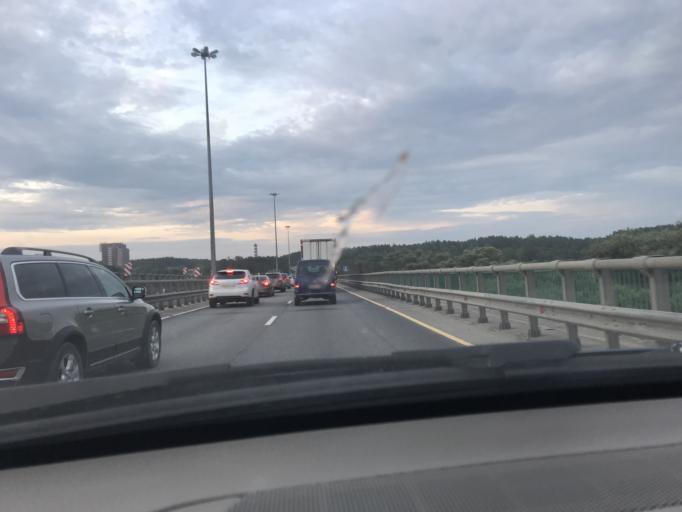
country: RU
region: Kaluga
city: Obninsk
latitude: 55.0491
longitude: 36.6082
